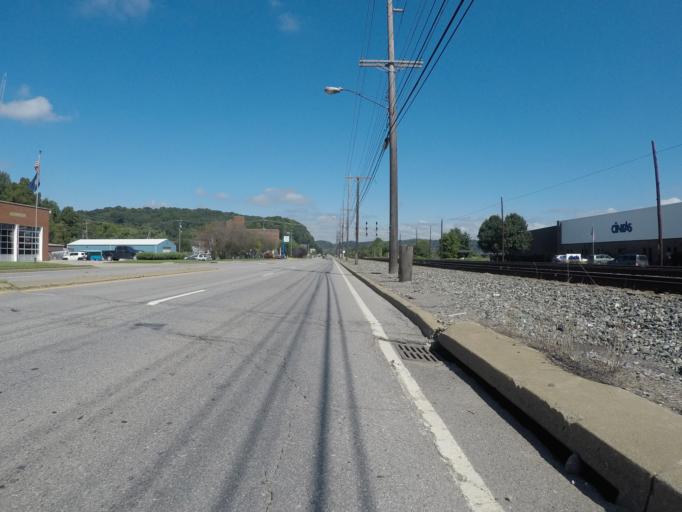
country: US
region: Kentucky
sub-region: Boyd County
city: Ashland
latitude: 38.4514
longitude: -82.6123
